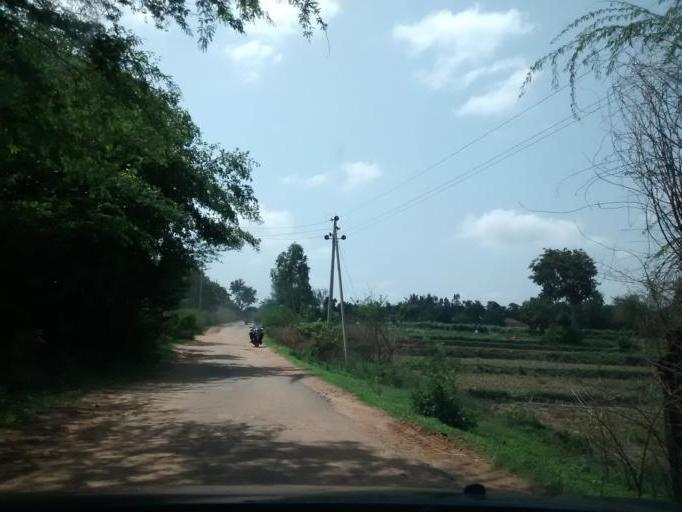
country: IN
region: Karnataka
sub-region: Hassan
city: Hole Narsipur
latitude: 12.6963
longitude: 76.1759
